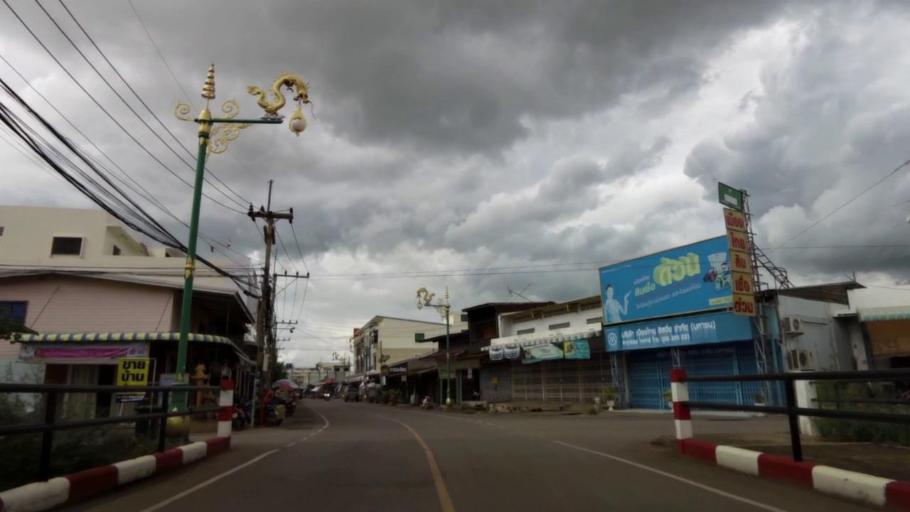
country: TH
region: Nakhon Sawan
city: Phai Sali
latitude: 15.5996
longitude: 100.6463
